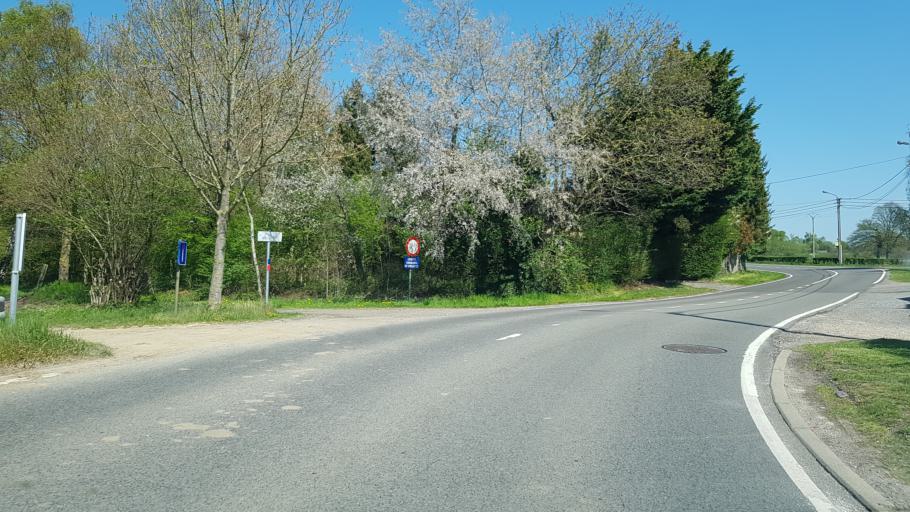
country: BE
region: Wallonia
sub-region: Province de Liege
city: Plombieres
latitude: 50.7427
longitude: 5.9705
